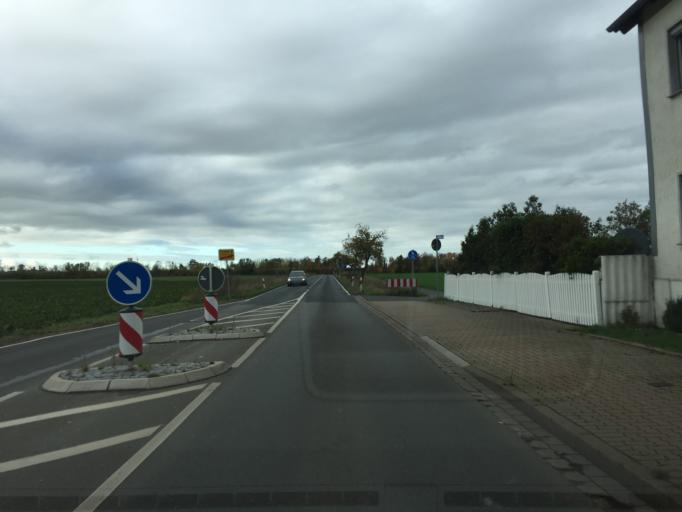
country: DE
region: Lower Saxony
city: Wolfenbuettel
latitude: 52.1751
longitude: 10.5138
